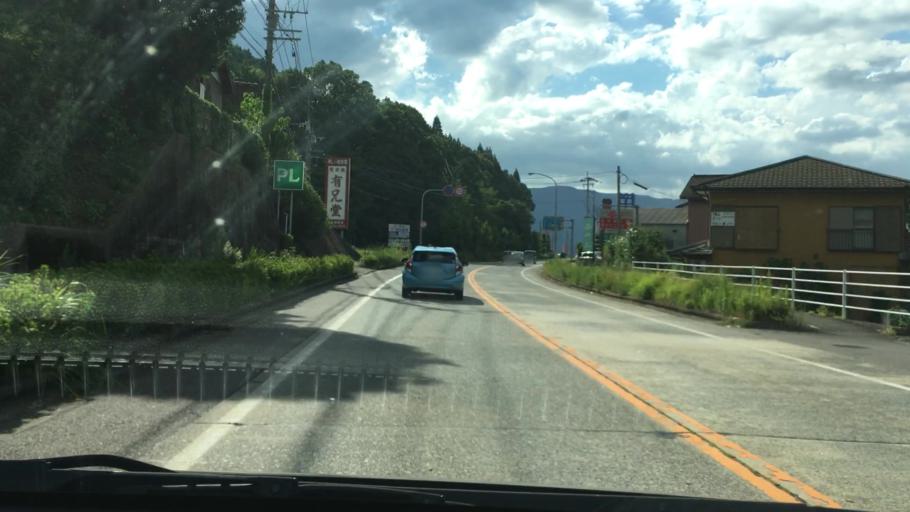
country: JP
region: Saga Prefecture
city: Imaricho-ko
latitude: 33.1822
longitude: 129.8769
